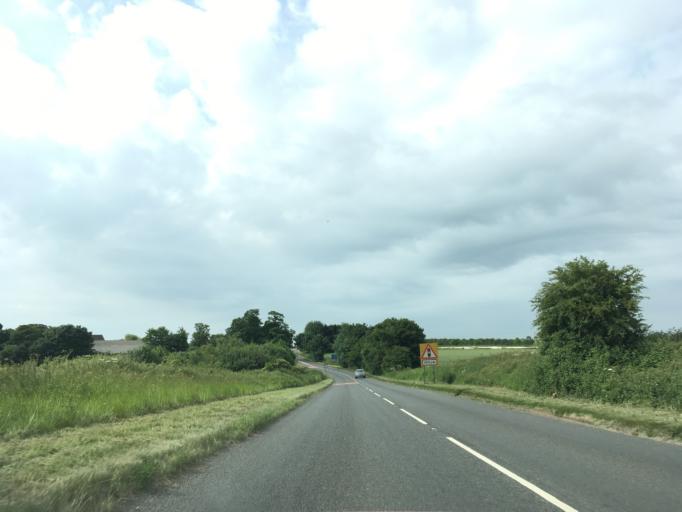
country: GB
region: England
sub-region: Gloucestershire
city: Nailsworth
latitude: 51.6565
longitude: -2.2337
